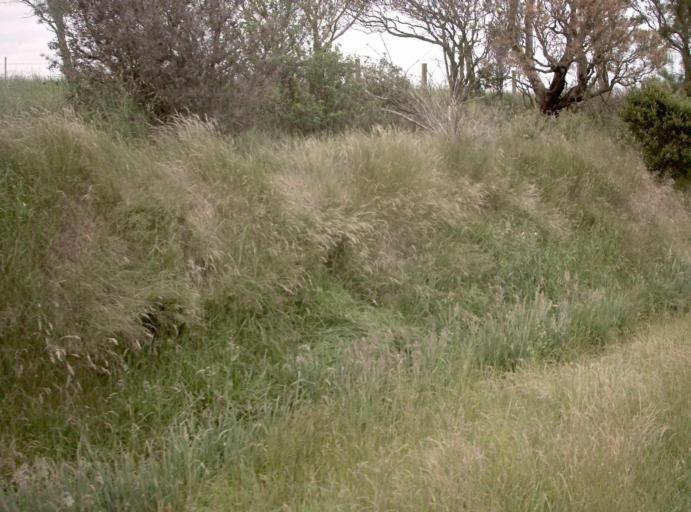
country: AU
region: Victoria
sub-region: Bass Coast
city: North Wonthaggi
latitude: -38.4604
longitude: 145.7892
